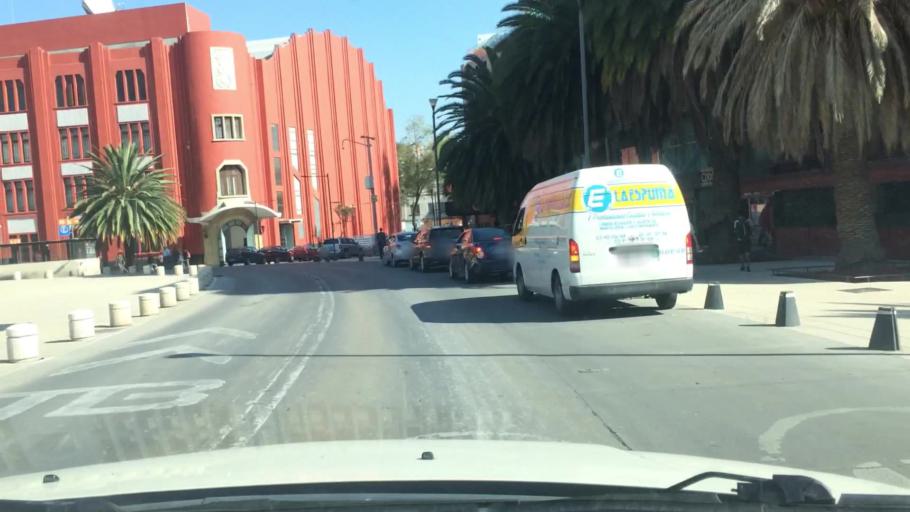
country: MX
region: Mexico City
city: Cuauhtemoc
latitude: 19.4361
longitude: -99.1530
